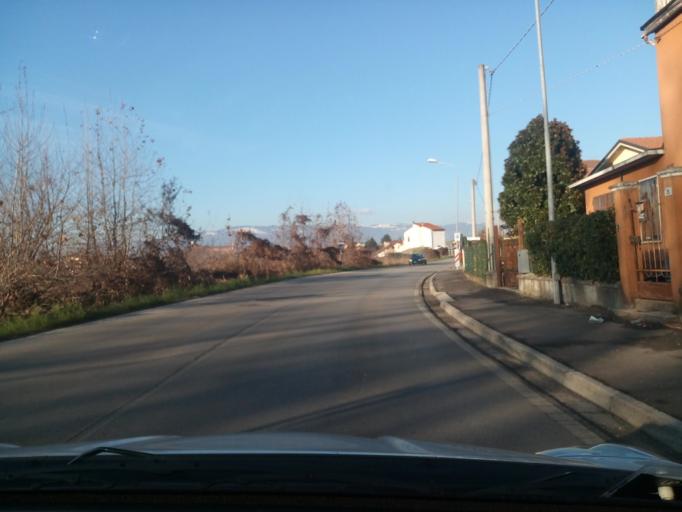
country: IT
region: Veneto
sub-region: Provincia di Vicenza
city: Dueville
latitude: 45.6286
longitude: 11.5511
